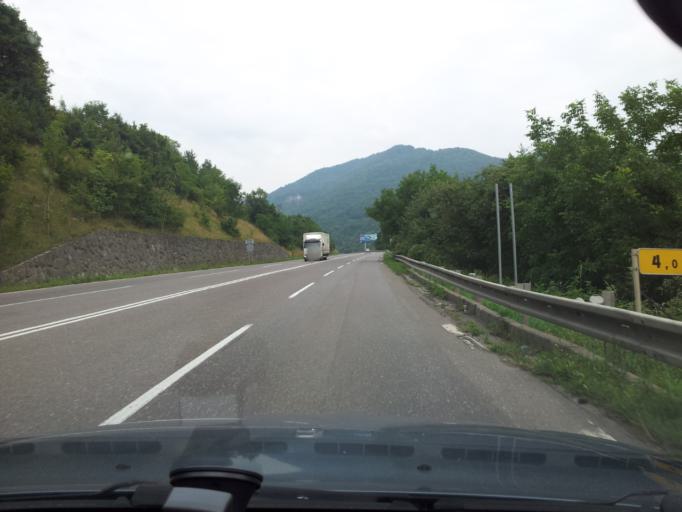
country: SK
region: Banskobystricky
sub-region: Okres Banska Bystrica
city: Banska Bystrica
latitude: 48.7608
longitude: 19.1392
